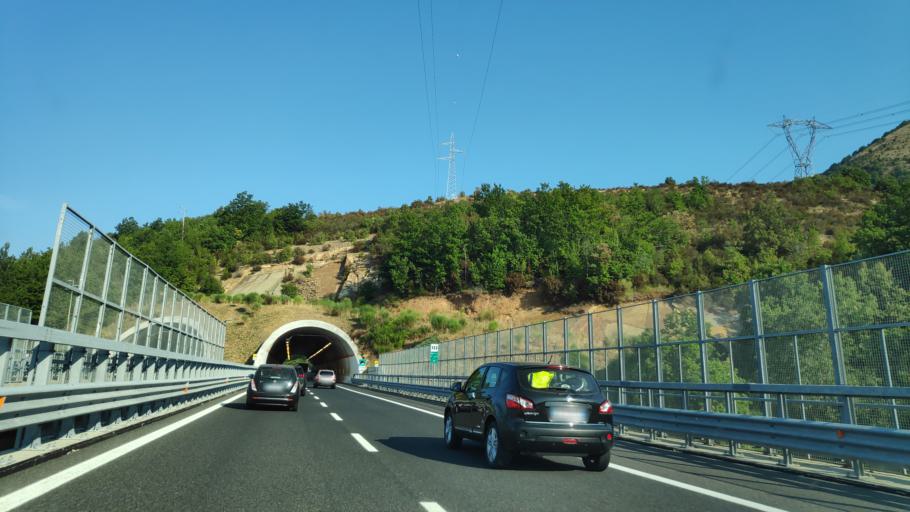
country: IT
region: Basilicate
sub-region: Provincia di Potenza
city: Lagonegro
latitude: 40.1252
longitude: 15.7794
